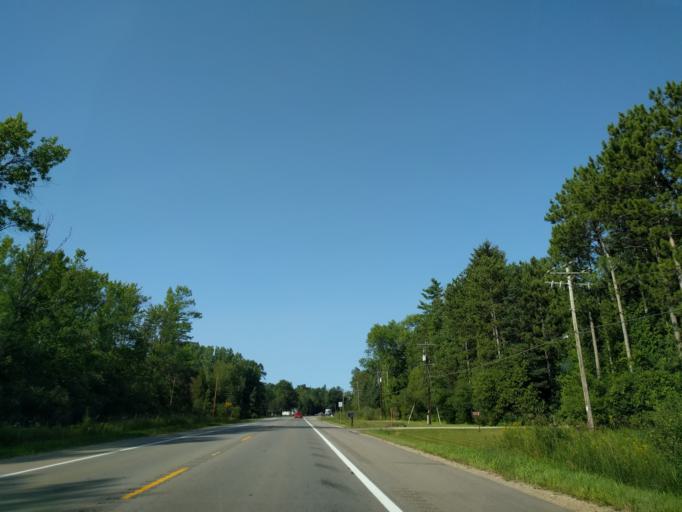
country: US
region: Michigan
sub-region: Menominee County
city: Menominee
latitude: 45.1604
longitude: -87.5905
